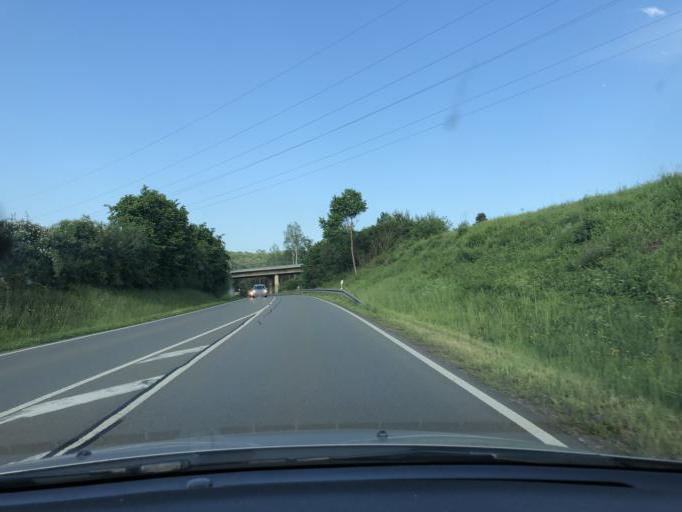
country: DE
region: Hesse
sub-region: Regierungsbezirk Kassel
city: Guxhagen
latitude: 51.1978
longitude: 9.4838
